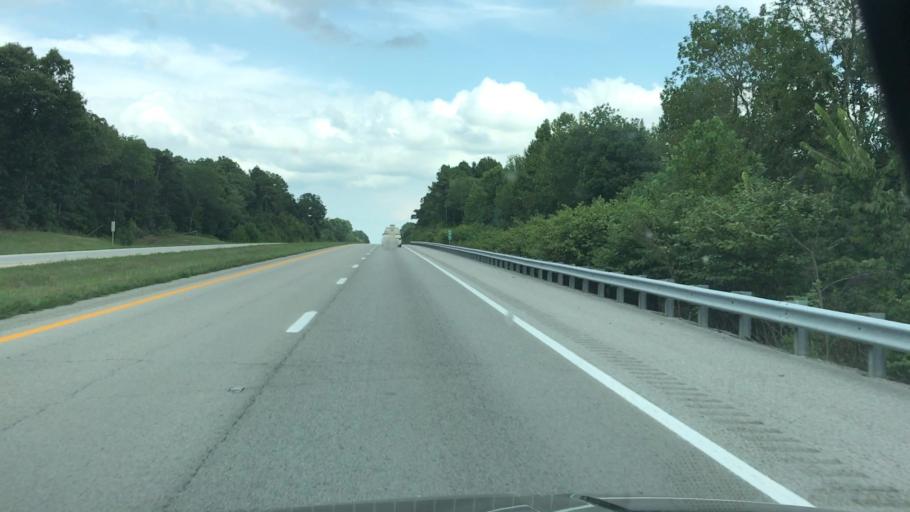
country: US
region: Kentucky
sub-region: Hopkins County
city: Dawson Springs
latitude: 37.1964
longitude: -87.6458
